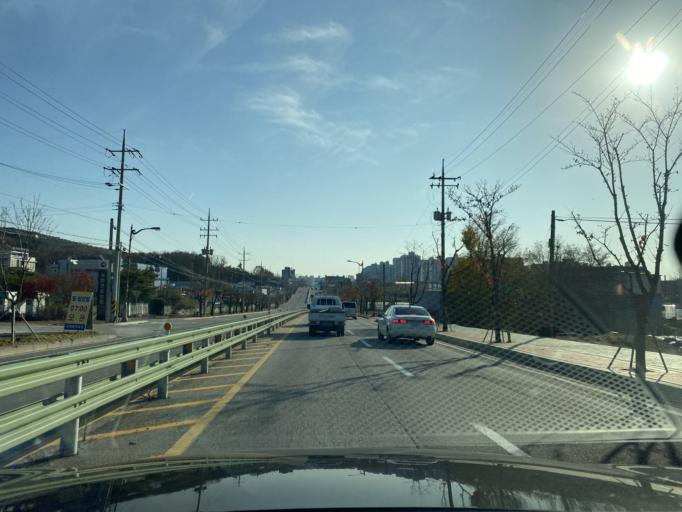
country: KR
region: Chungcheongnam-do
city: Yesan
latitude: 36.7027
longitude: 126.8386
